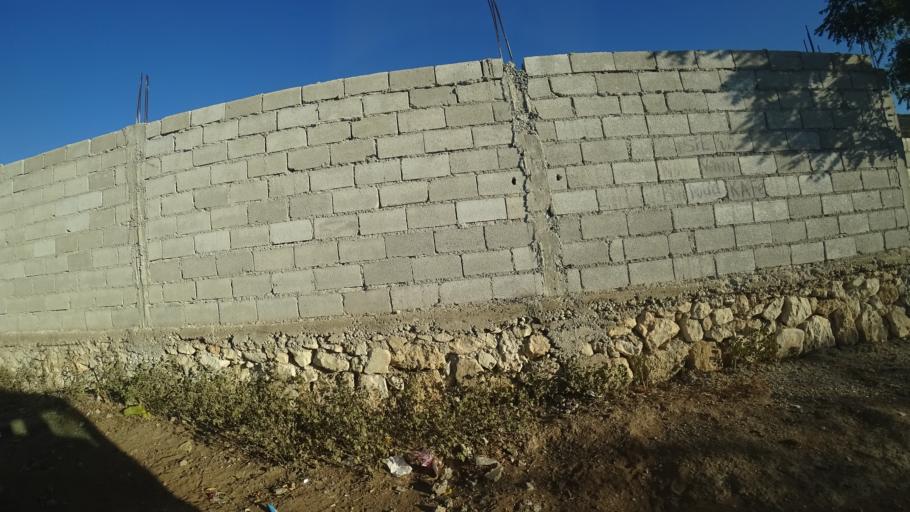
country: HT
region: Ouest
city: Croix des Bouquets
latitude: 18.6616
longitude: -72.2226
